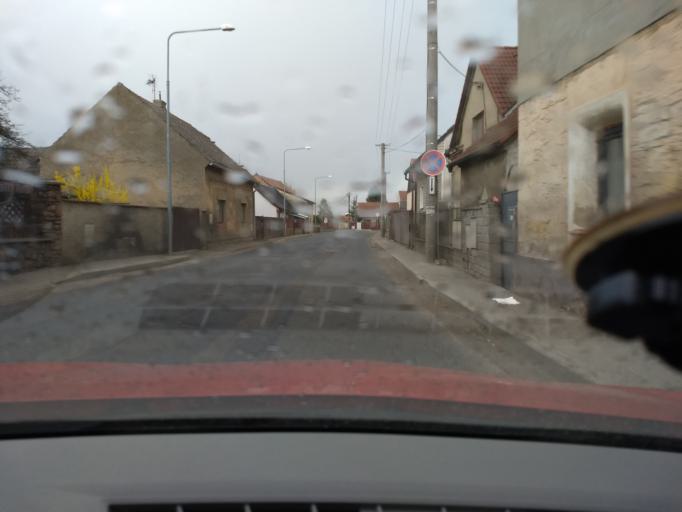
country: CZ
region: Central Bohemia
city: Rudna
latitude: 50.0408
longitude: 14.1875
